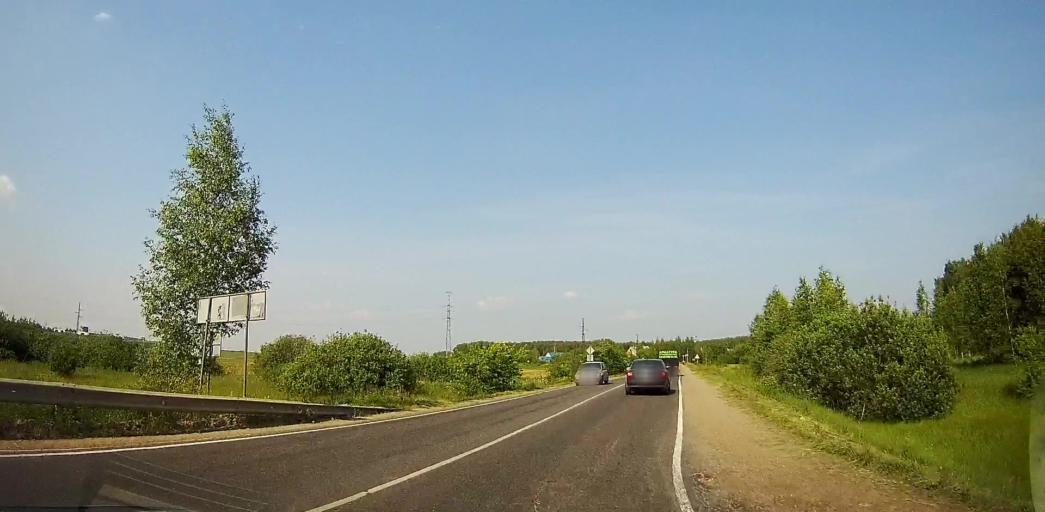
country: RU
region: Moskovskaya
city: Zhitnevo
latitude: 55.3256
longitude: 37.8990
